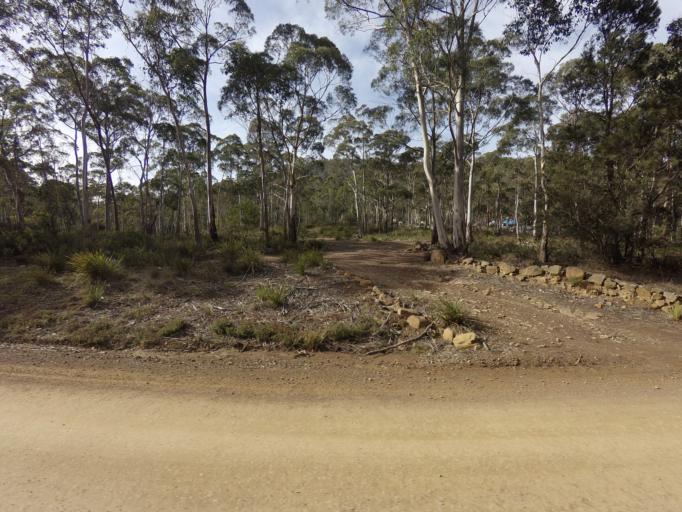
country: AU
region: Tasmania
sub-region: Huon Valley
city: Huonville
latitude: -43.0634
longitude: 147.0892
